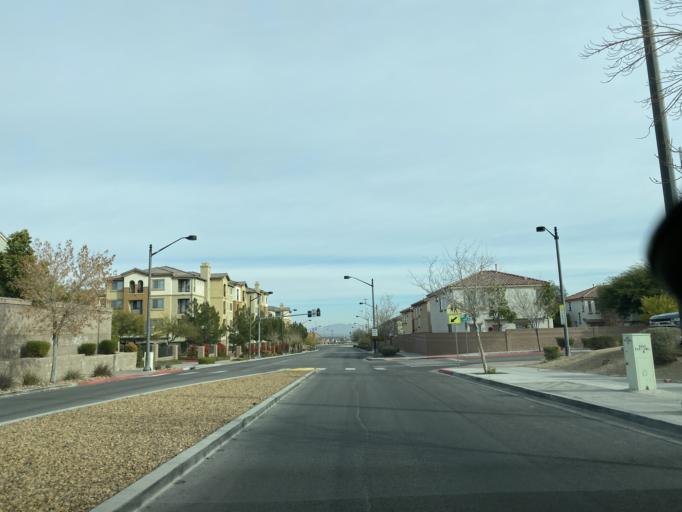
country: US
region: Nevada
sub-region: Clark County
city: Summerlin South
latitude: 36.2955
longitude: -115.2928
